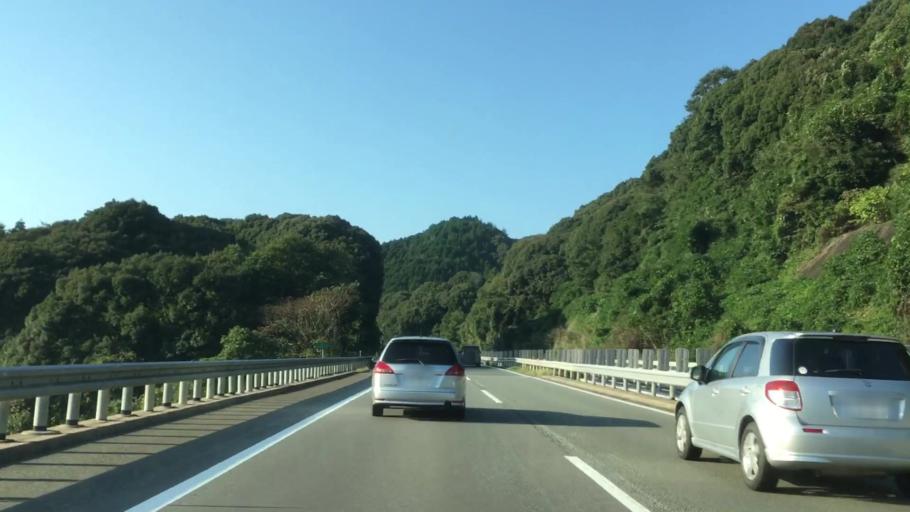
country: JP
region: Yamaguchi
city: Ogori-shimogo
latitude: 34.1322
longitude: 131.3764
